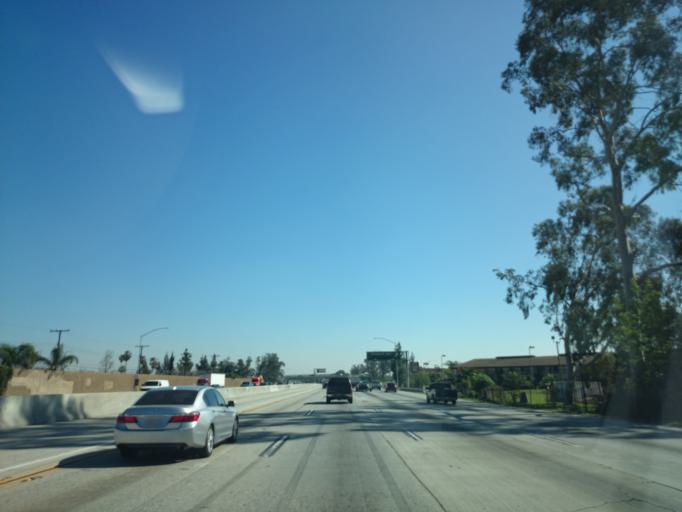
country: US
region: California
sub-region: San Bernardino County
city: Ontario
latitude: 34.0729
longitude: -117.6154
